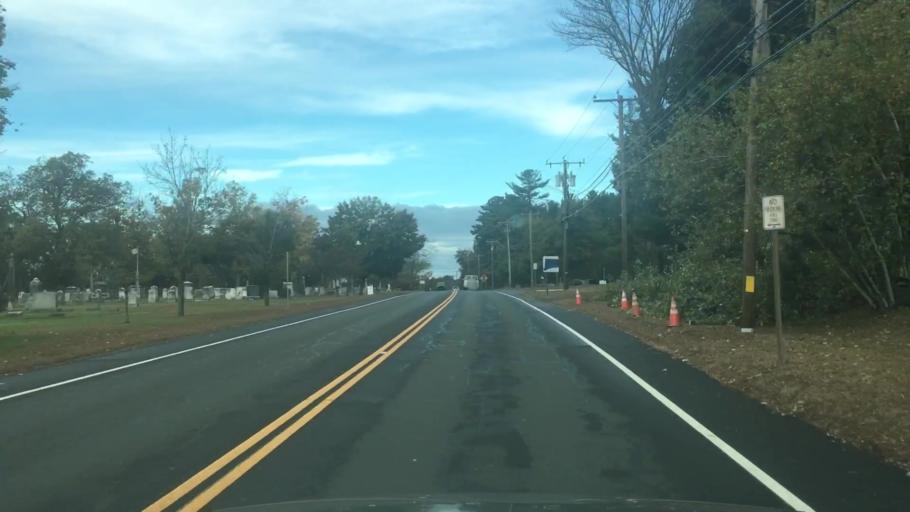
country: US
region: Connecticut
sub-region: Tolland County
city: Somers
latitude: 41.9841
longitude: -72.4583
